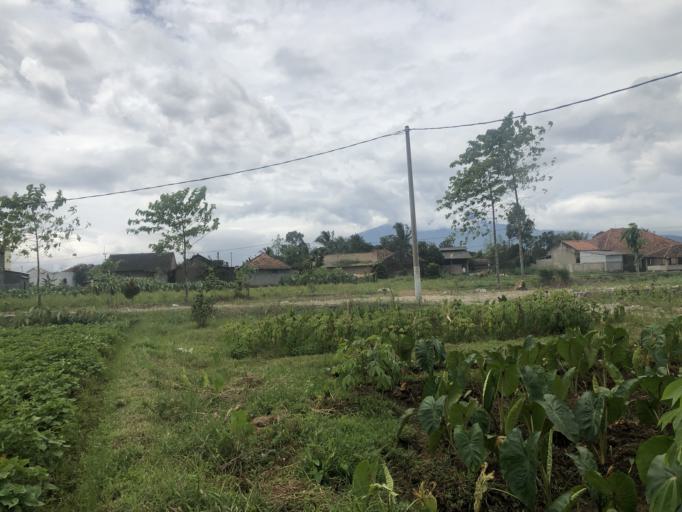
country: ID
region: West Java
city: Ciampea
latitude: -6.5502
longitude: 106.7399
